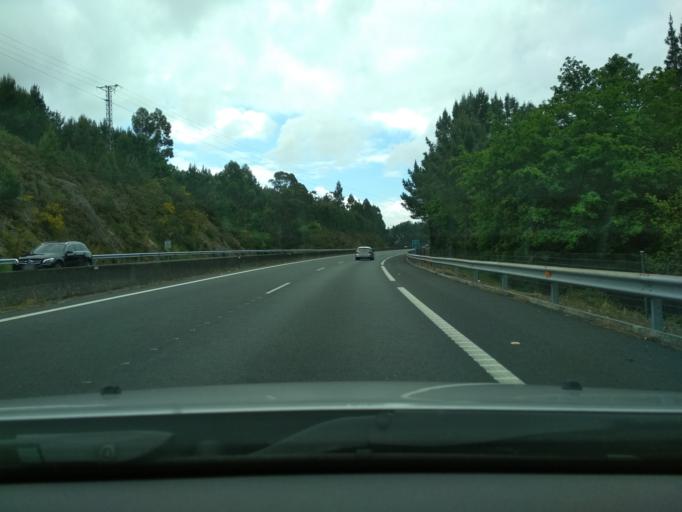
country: ES
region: Galicia
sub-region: Provincia da Coruna
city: Padron
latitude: 42.7872
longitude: -8.6431
